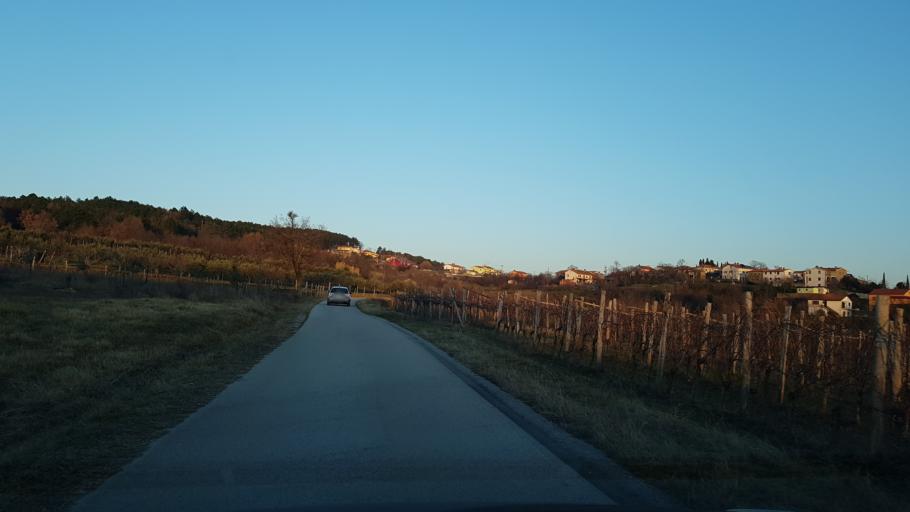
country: SI
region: Koper-Capodistria
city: Sv. Anton
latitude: 45.4971
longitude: 13.8494
